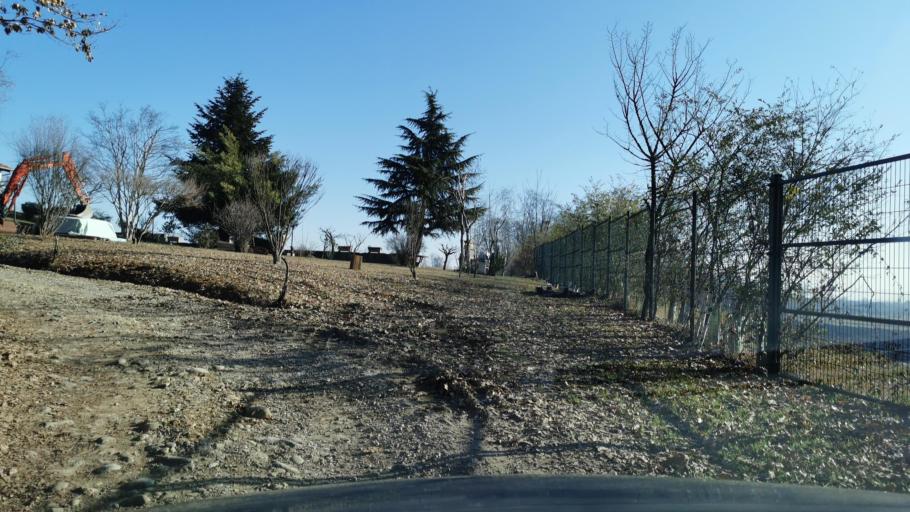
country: IT
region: Piedmont
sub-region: Provincia di Torino
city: Leini
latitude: 45.2134
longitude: 7.6941
